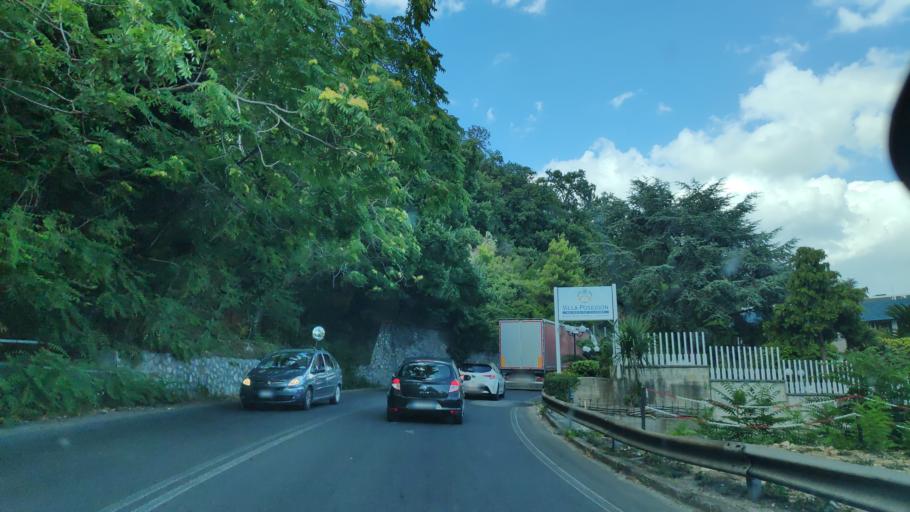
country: IT
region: Campania
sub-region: Provincia di Salerno
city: Vietri sul Mare
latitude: 40.6800
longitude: 14.7489
